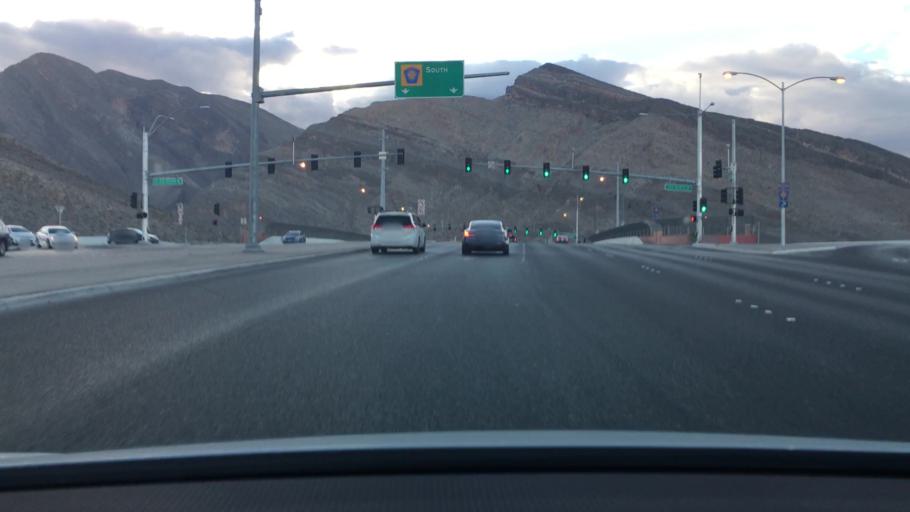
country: US
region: Nevada
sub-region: Clark County
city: Summerlin South
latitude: 36.2187
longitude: -115.3262
